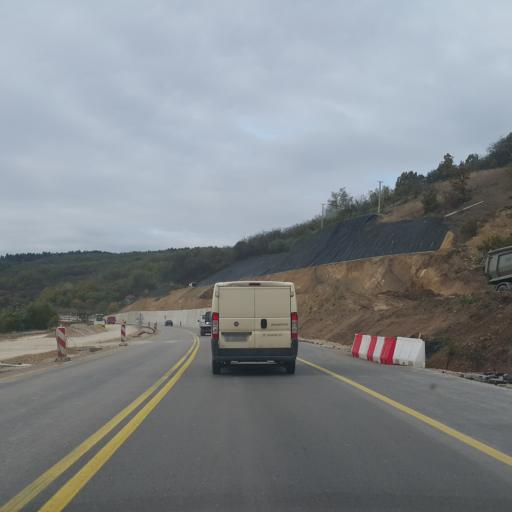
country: RS
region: Central Serbia
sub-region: Pirotski Okrug
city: Bela Palanka
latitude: 43.2316
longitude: 22.4586
